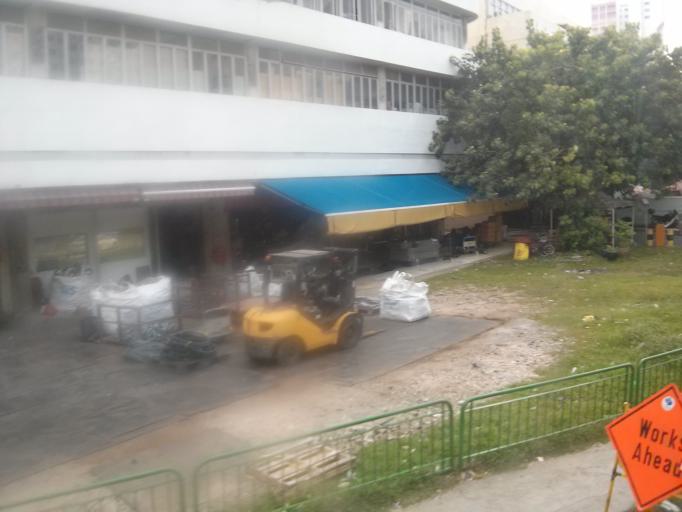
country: SG
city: Singapore
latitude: 1.3065
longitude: 103.8587
